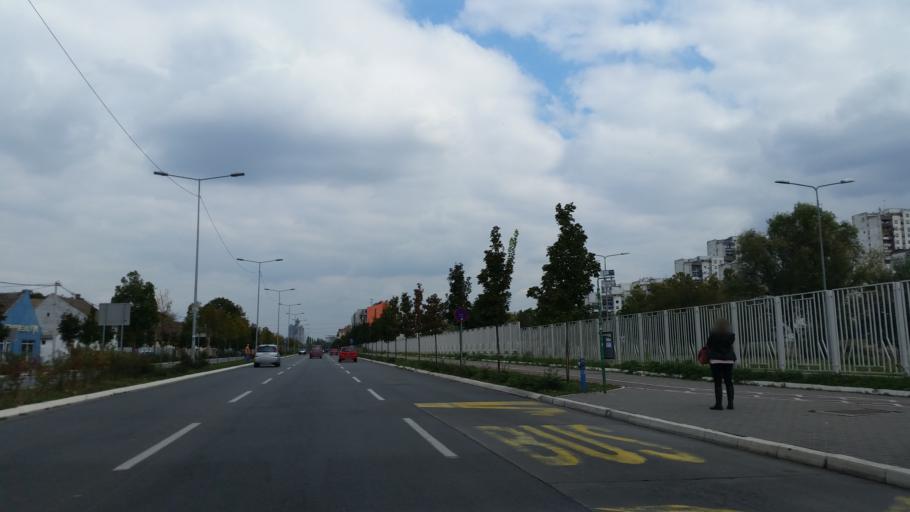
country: RS
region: Central Serbia
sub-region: Belgrade
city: Zemun
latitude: 44.8080
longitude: 20.3770
